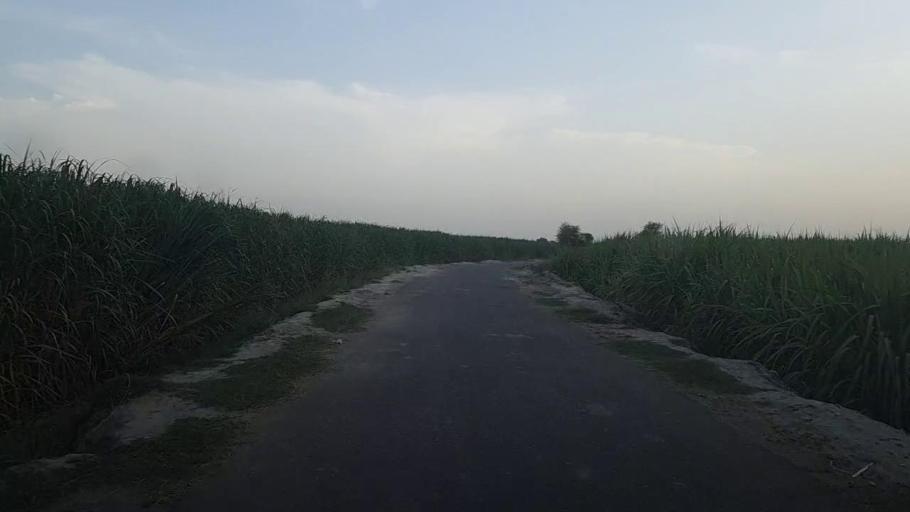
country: PK
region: Sindh
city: Ubauro
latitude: 28.3569
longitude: 69.7841
